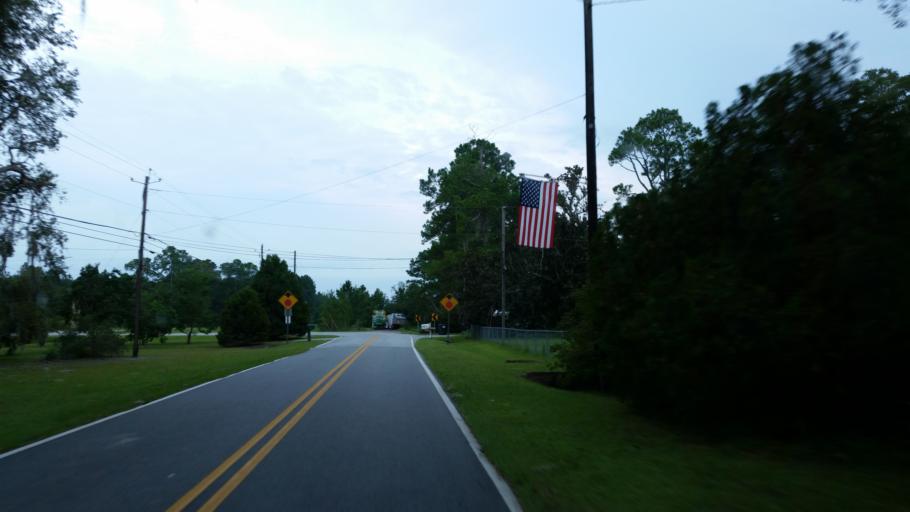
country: US
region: Georgia
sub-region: Lowndes County
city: Valdosta
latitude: 30.7447
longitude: -83.2206
